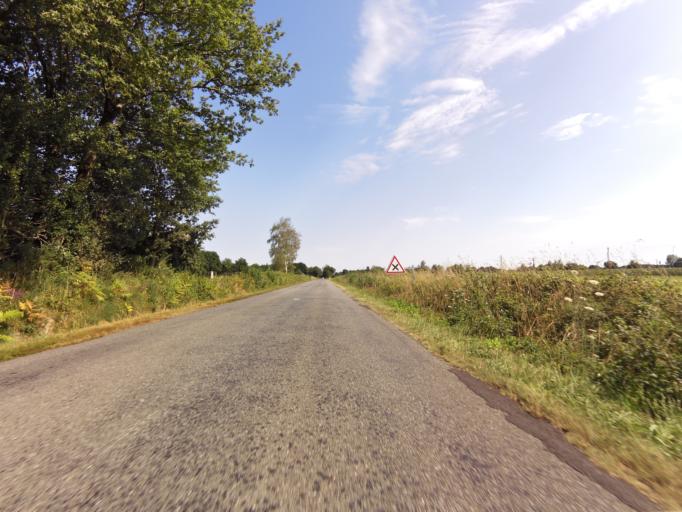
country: FR
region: Brittany
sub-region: Departement du Morbihan
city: Limerzel
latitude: 47.6490
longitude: -2.3813
